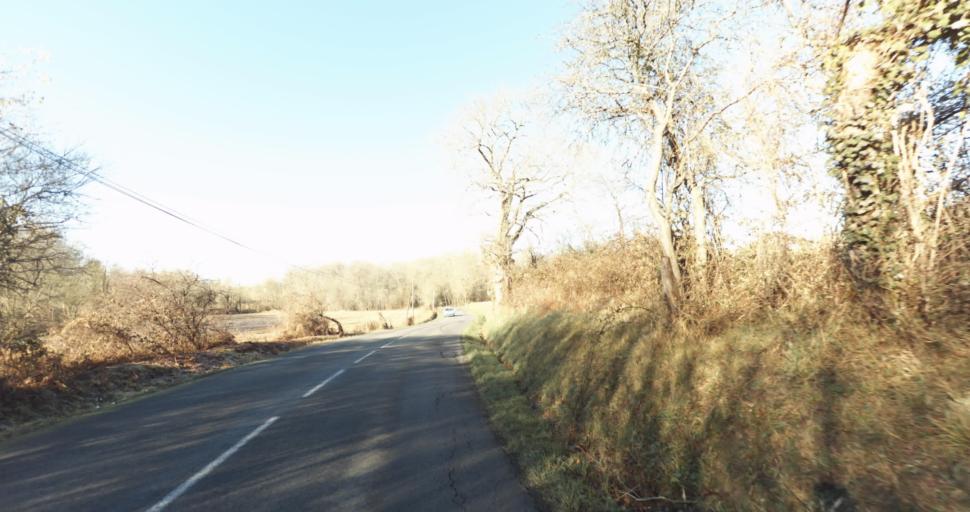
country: FR
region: Aquitaine
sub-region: Departement des Pyrenees-Atlantiques
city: Morlaas
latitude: 43.3377
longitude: -0.2413
